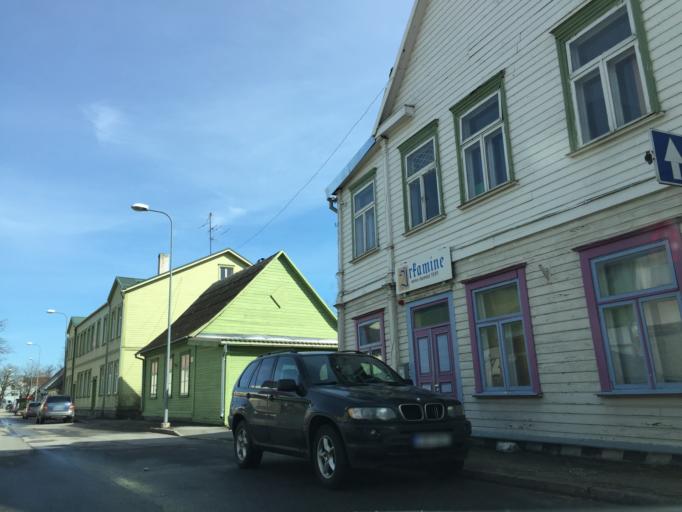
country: EE
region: Paernumaa
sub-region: Paernu linn
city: Parnu
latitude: 58.3814
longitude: 24.5123
